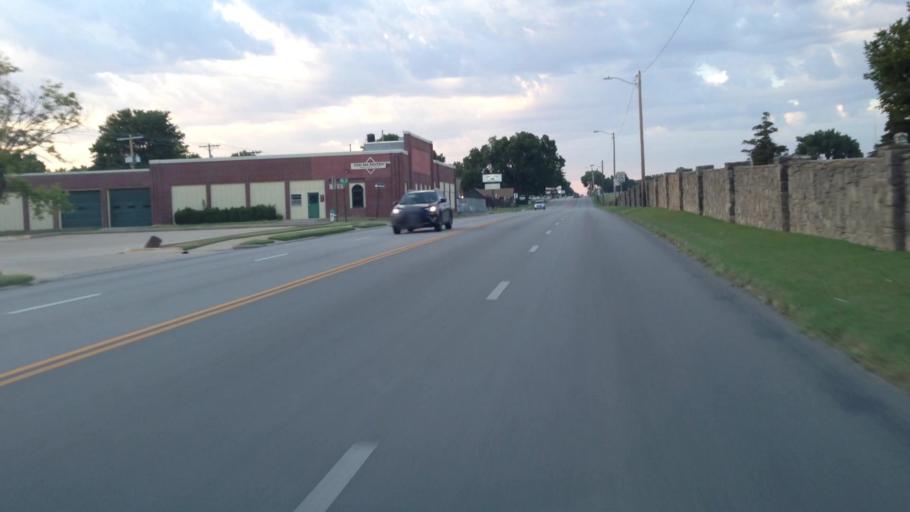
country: US
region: Kansas
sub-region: Montgomery County
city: Independence
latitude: 37.2382
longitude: -95.7062
